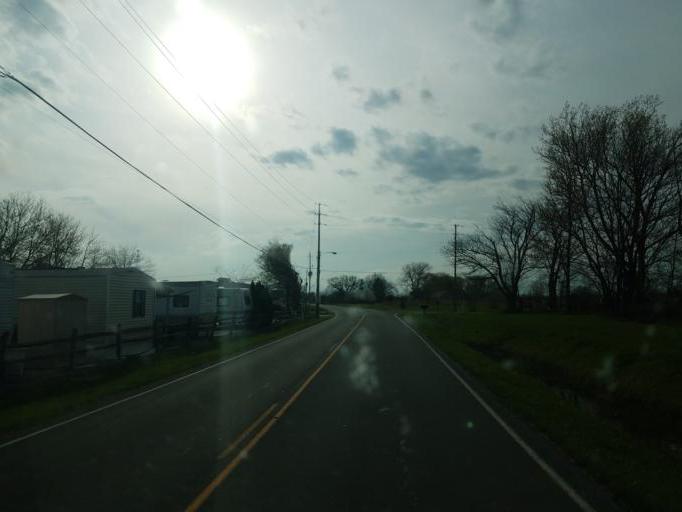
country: US
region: Ohio
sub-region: Erie County
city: Sandusky
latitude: 41.5079
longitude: -82.7798
